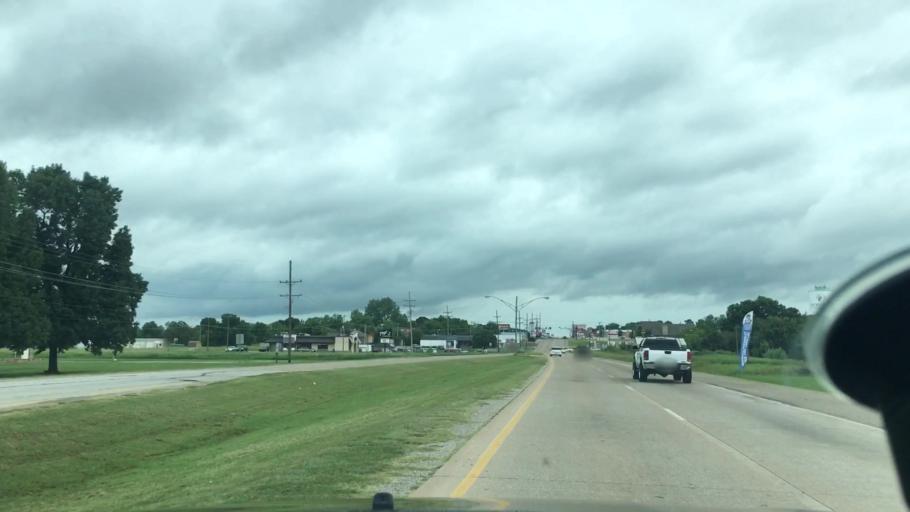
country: US
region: Oklahoma
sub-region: Seminole County
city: Seminole
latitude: 35.2372
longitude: -96.6712
